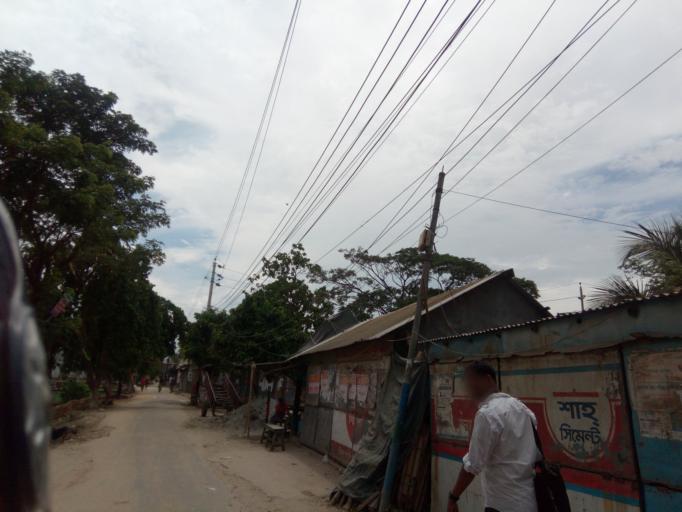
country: BD
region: Dhaka
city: Paltan
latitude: 23.7560
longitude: 90.4563
